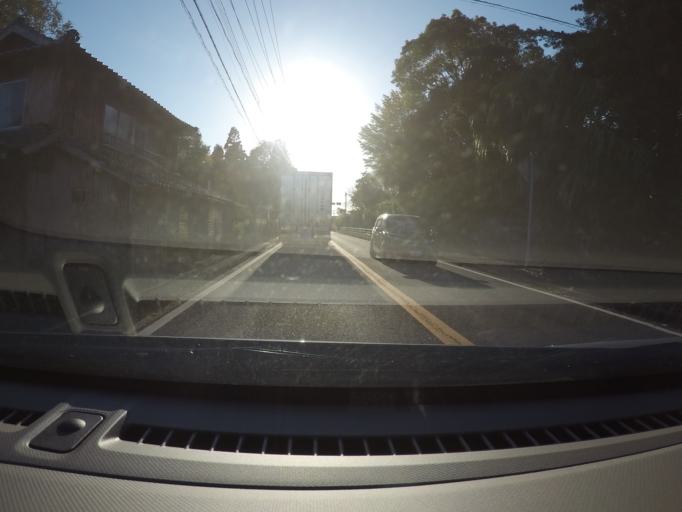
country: JP
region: Kagoshima
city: Izumi
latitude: 32.0859
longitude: 130.2812
